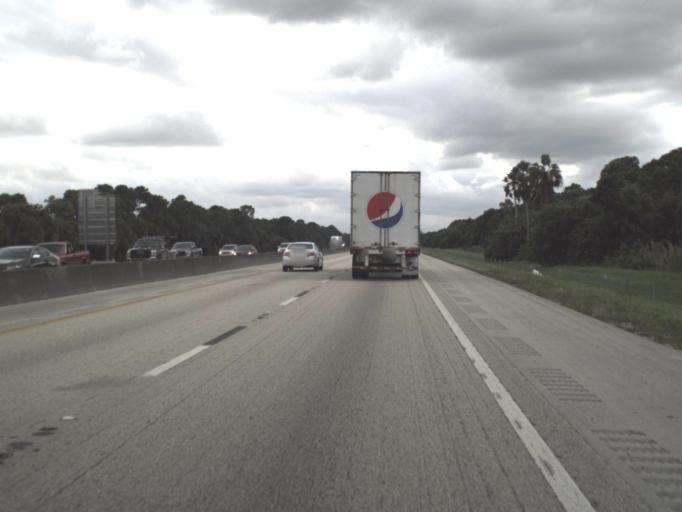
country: US
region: Florida
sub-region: Palm Beach County
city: Palm Beach Gardens
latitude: 26.7844
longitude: -80.1323
